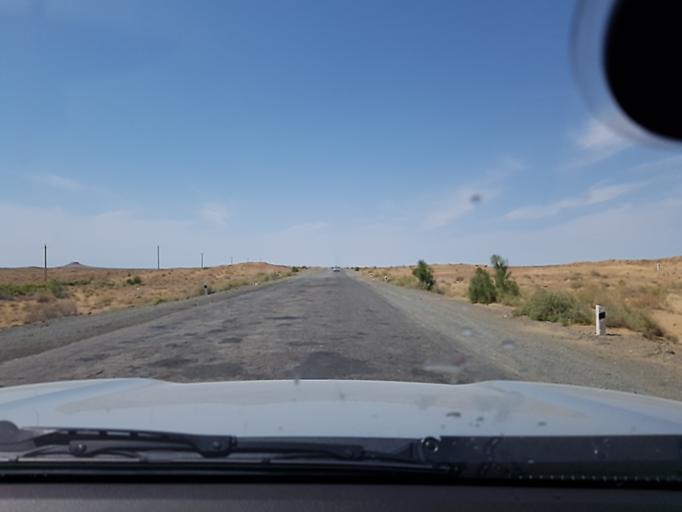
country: UZ
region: Karakalpakstan
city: Mang'it Shahri
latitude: 42.2539
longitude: 60.1362
